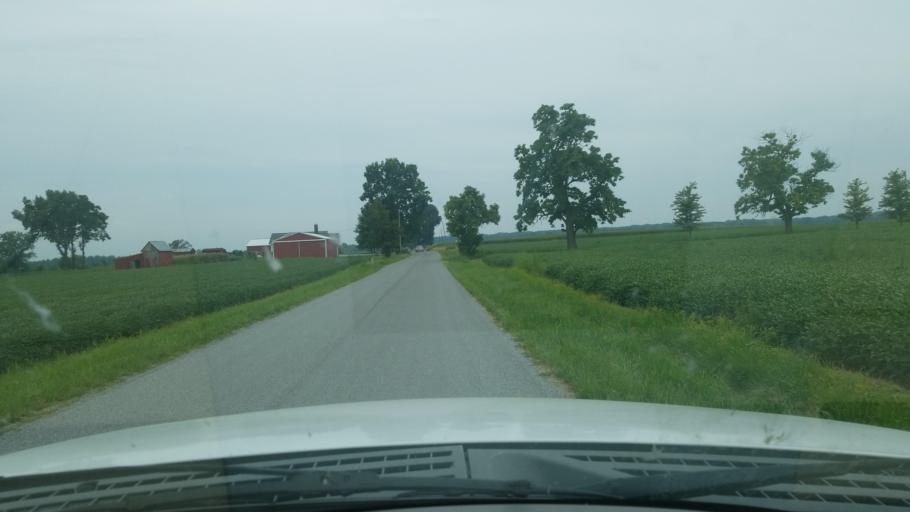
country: US
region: Illinois
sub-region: Saline County
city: Eldorado
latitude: 37.8653
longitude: -88.4851
